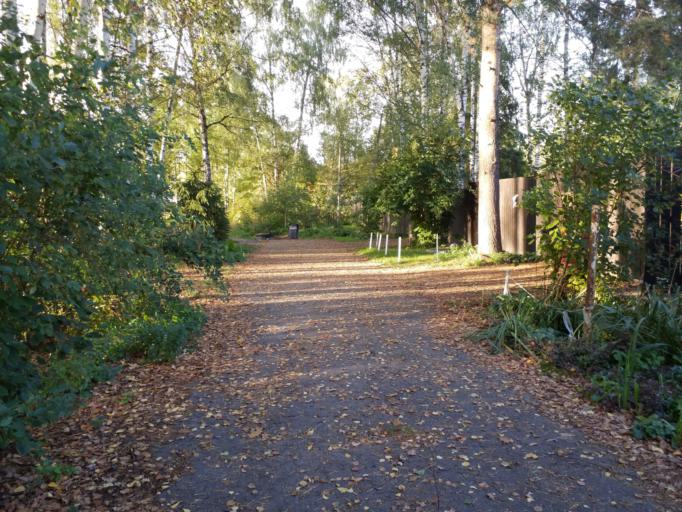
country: RU
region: Moskovskaya
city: Ashukino
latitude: 56.1663
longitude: 37.9554
